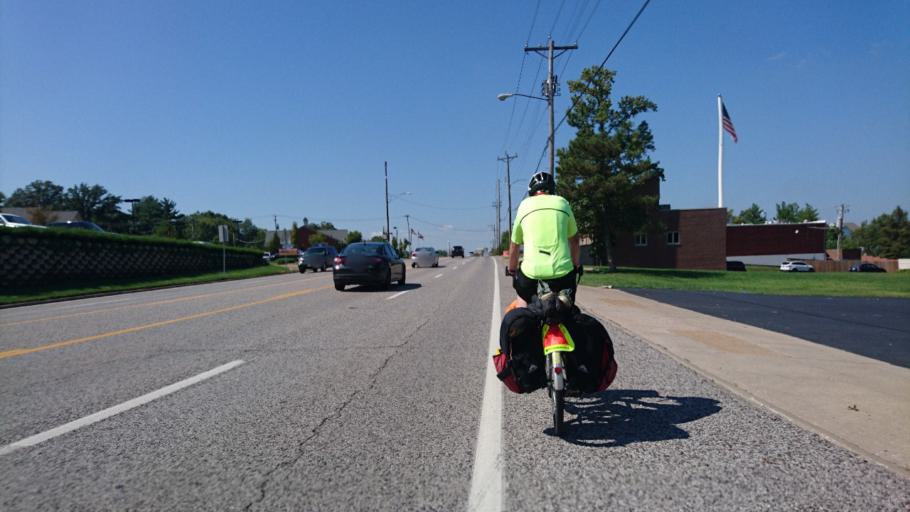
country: US
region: Missouri
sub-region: Saint Louis County
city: Des Peres
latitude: 38.5997
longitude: -90.4256
